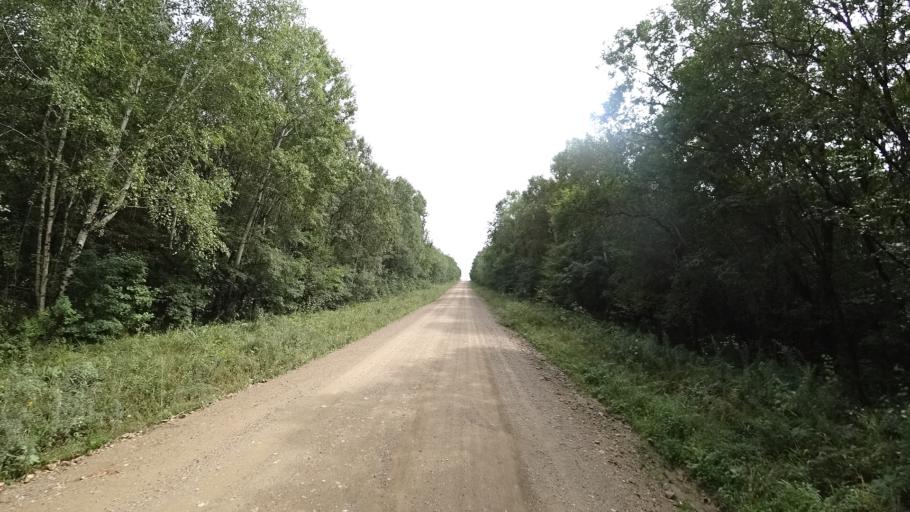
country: RU
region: Primorskiy
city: Lyalichi
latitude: 44.0967
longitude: 132.4301
